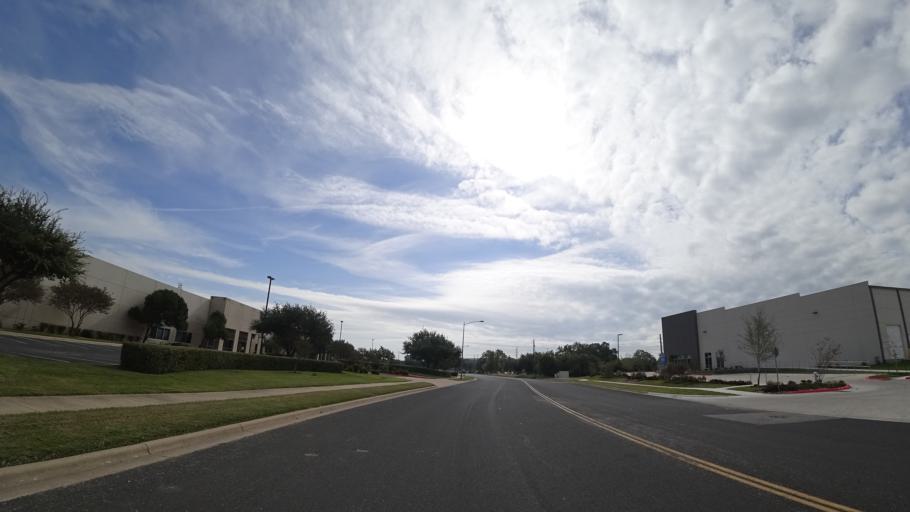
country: US
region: Texas
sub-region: Travis County
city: Austin
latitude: 30.2094
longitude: -97.7169
